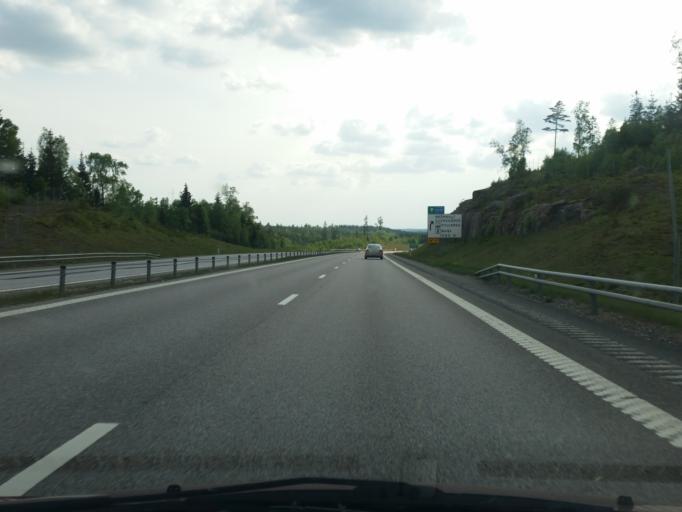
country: SE
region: Vaestra Goetaland
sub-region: Boras Kommun
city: Ganghester
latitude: 57.7341
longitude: 13.0373
